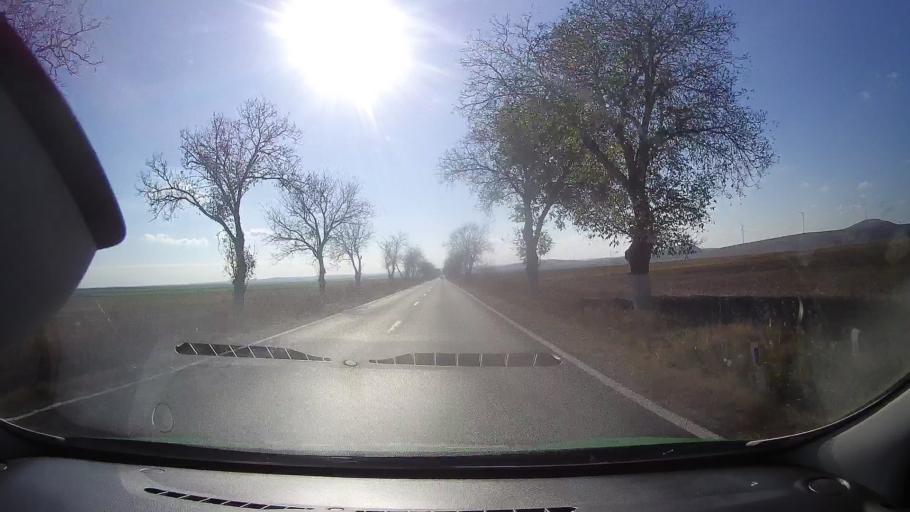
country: RO
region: Tulcea
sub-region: Comuna Ceamurlia de Jos
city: Ceamurlia de Jos
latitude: 44.7968
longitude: 28.6903
